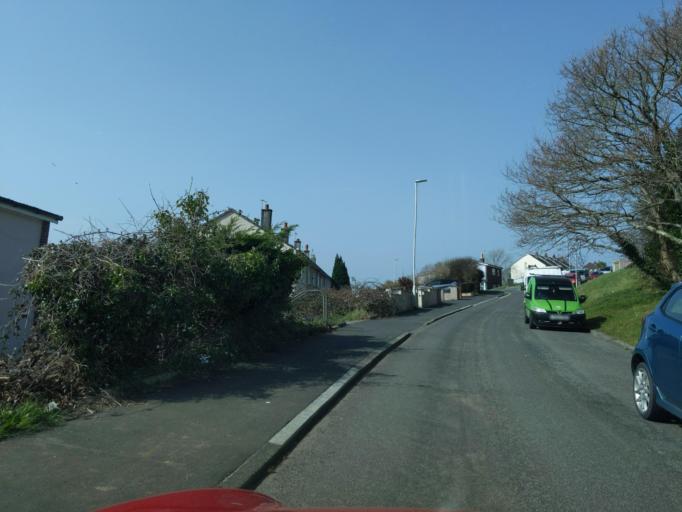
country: GB
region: England
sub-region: Plymouth
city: Plymouth
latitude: 50.4253
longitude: -4.1410
